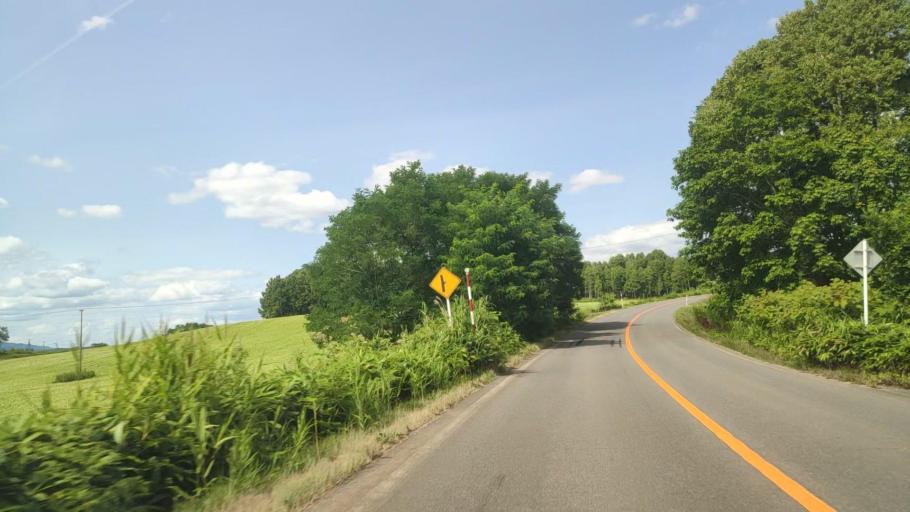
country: JP
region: Hokkaido
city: Nayoro
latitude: 44.2789
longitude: 142.4232
